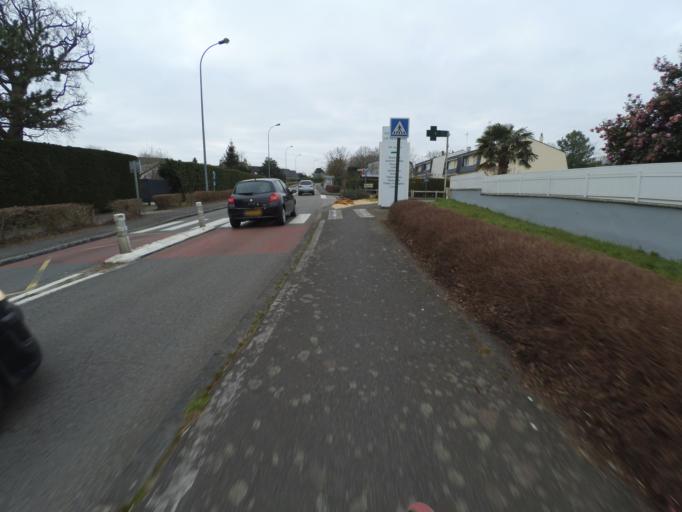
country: FR
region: Pays de la Loire
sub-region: Departement de la Loire-Atlantique
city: Carquefou
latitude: 47.2782
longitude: -1.4846
